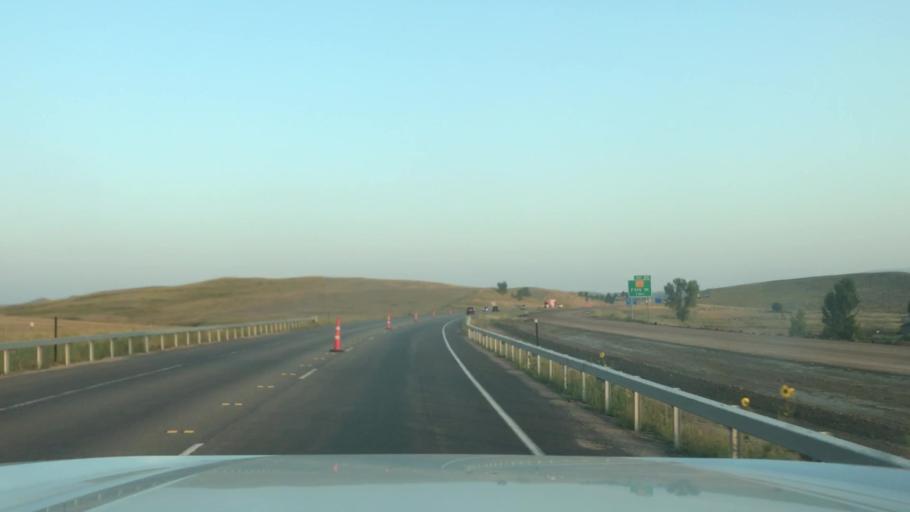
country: US
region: Wyoming
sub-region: Sheridan County
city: Sheridan
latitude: 44.8211
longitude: -106.9416
